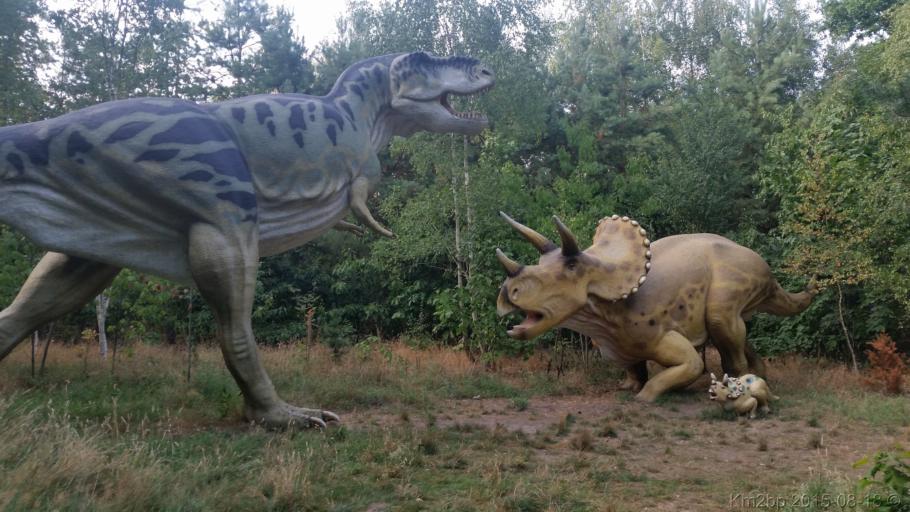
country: PL
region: Lubusz
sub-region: Powiat gorzowski
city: Bogdaniec
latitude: 52.6708
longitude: 14.9976
